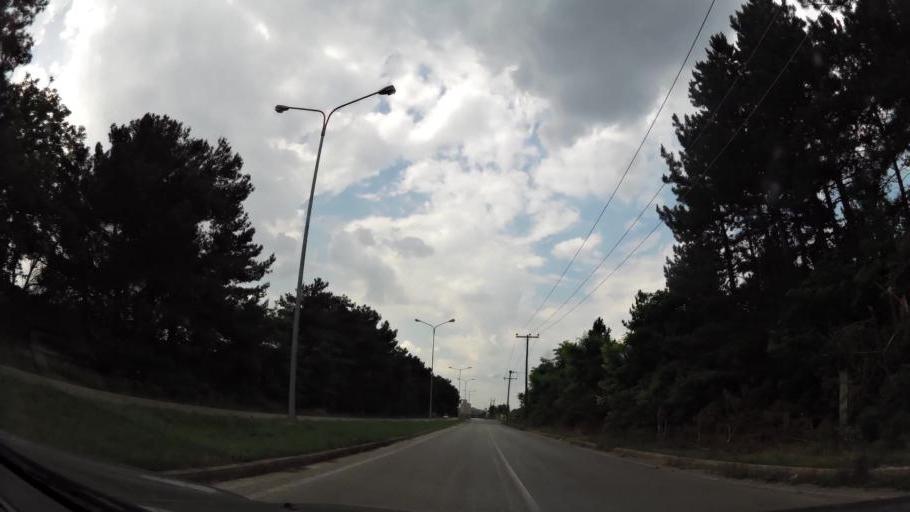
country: GR
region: West Macedonia
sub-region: Nomos Kozanis
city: Koila
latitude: 40.3326
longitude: 21.8267
